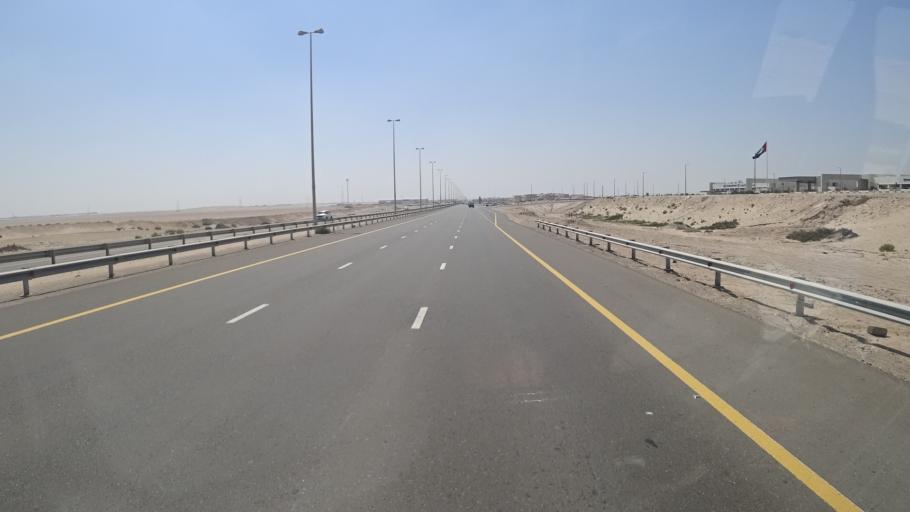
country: AE
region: Abu Dhabi
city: Abu Dhabi
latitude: 24.3228
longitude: 54.6859
